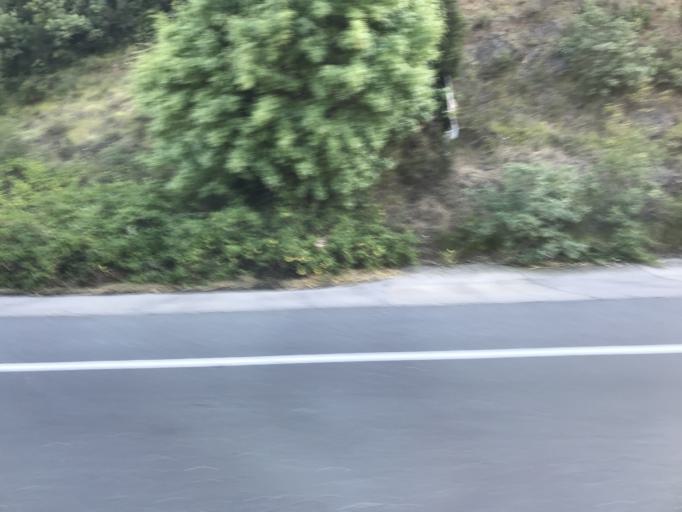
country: TR
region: Kocaeli
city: Gebze
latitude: 40.7744
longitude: 29.4237
